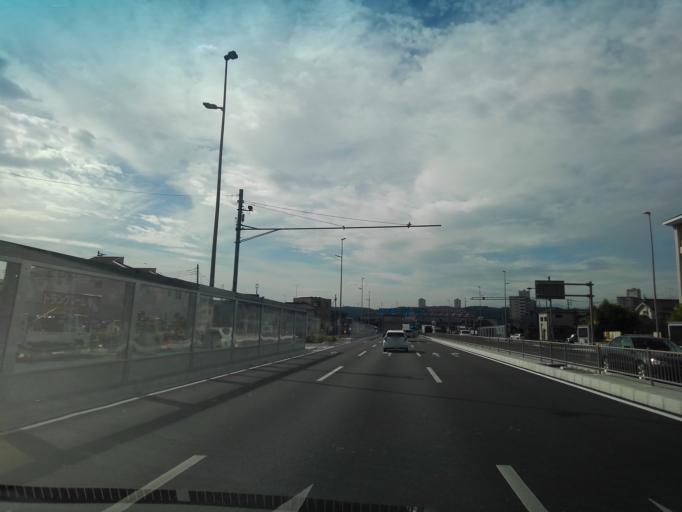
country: JP
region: Tokyo
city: Fussa
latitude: 35.7158
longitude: 139.3392
